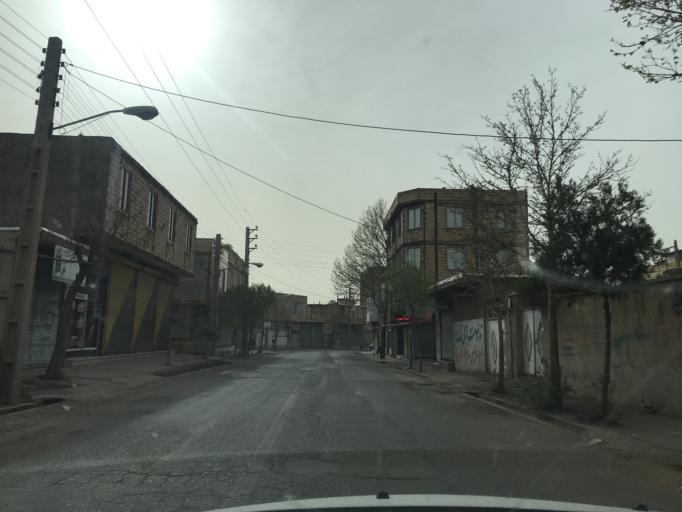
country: IR
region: Qazvin
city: Takestan
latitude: 36.0681
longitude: 49.6885
